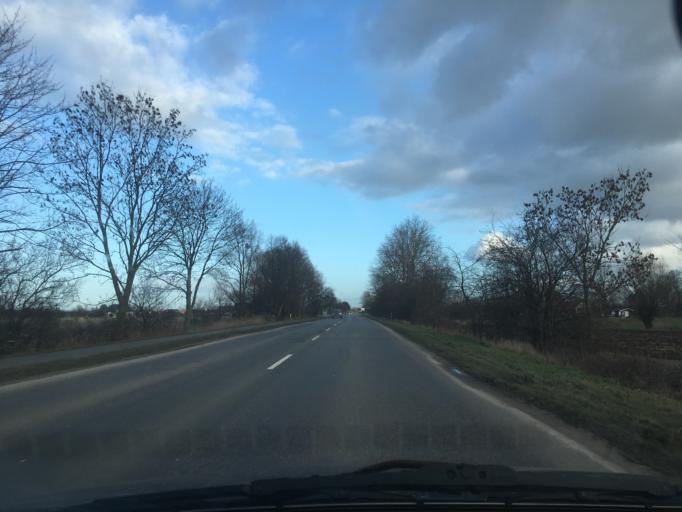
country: PL
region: Pomeranian Voivodeship
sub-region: Powiat gdanski
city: Cedry Wielkie
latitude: 54.3297
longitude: 18.7791
